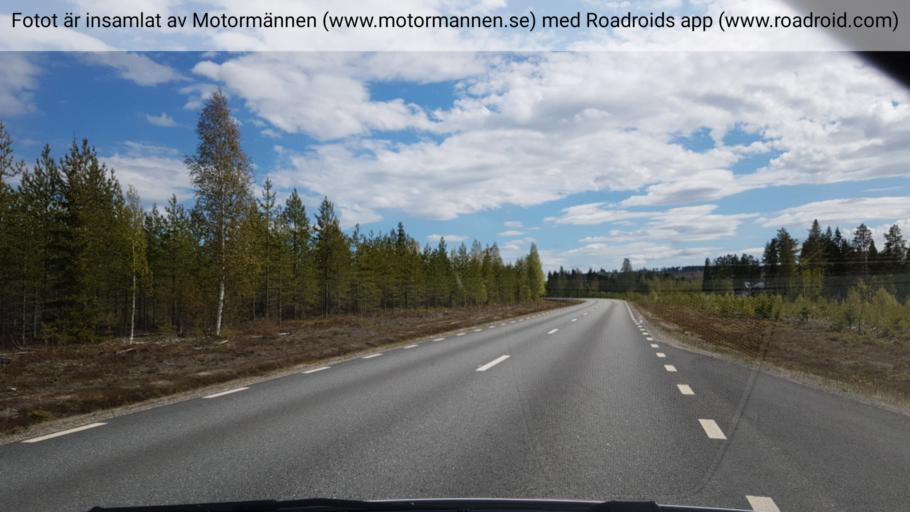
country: SE
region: Vaesterbotten
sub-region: Bjurholms Kommun
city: Bjurholm
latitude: 64.2973
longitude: 19.1778
